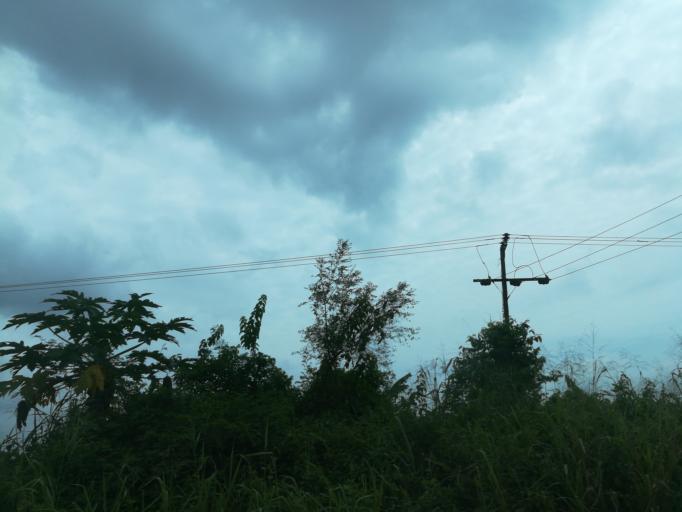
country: NG
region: Lagos
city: Ejirin
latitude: 6.6549
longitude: 3.7124
